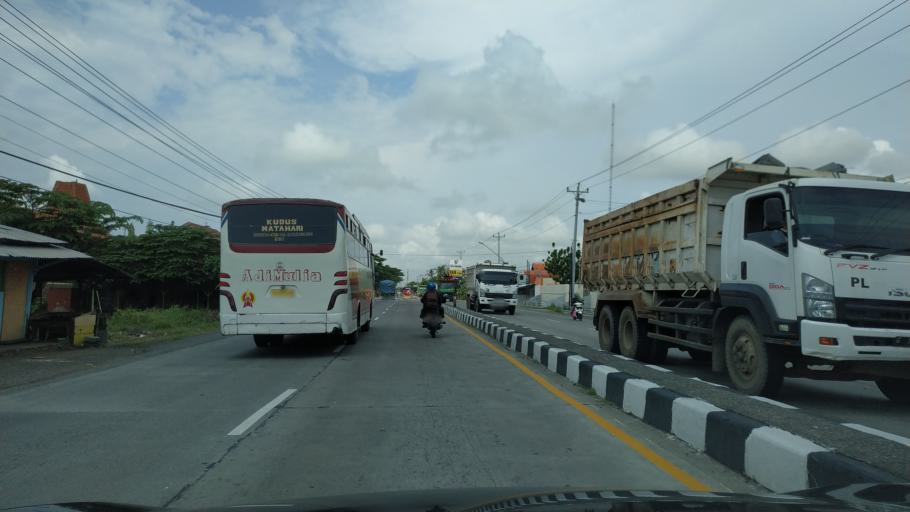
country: ID
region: Central Java
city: Tarub
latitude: -6.8714
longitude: 109.2390
